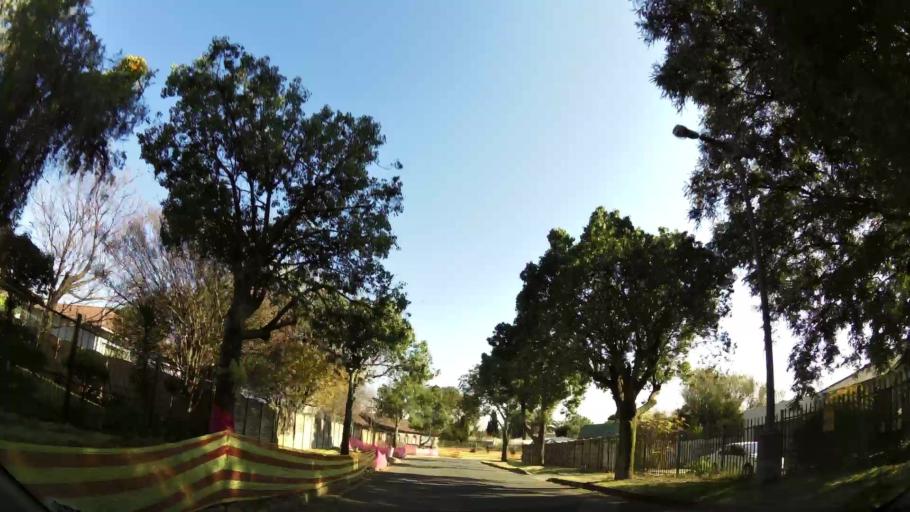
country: ZA
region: Gauteng
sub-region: Ekurhuleni Metropolitan Municipality
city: Benoni
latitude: -26.1530
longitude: 28.3109
